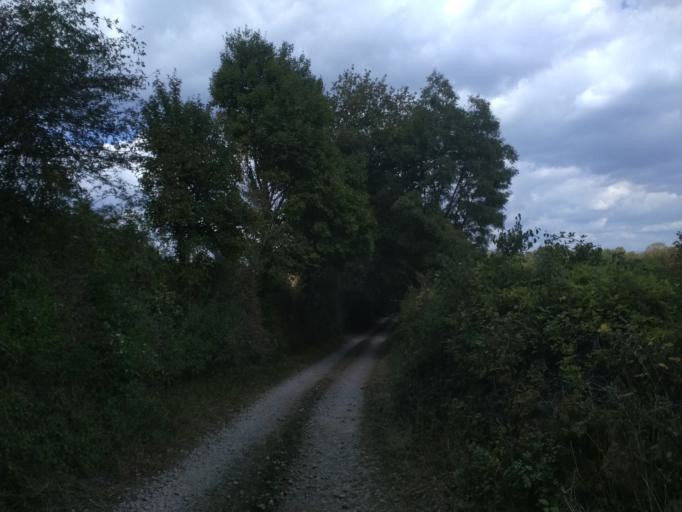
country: FR
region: Midi-Pyrenees
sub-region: Departement de l'Aveyron
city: Bozouls
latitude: 44.4694
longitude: 2.6763
